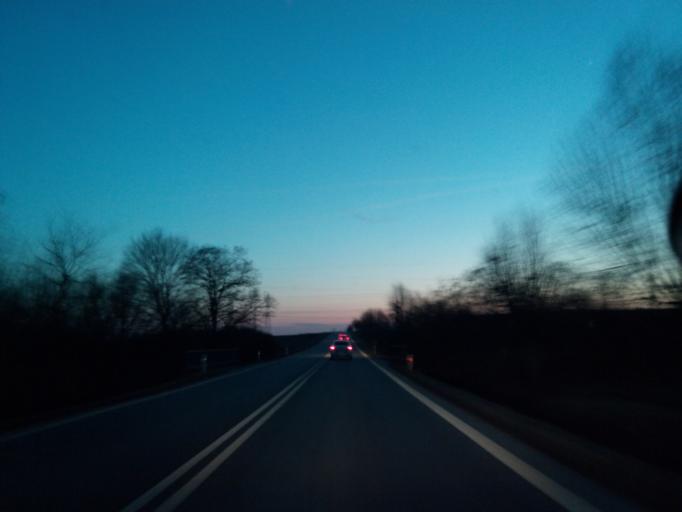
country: SK
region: Kosicky
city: Michalovce
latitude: 48.7131
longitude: 21.8356
